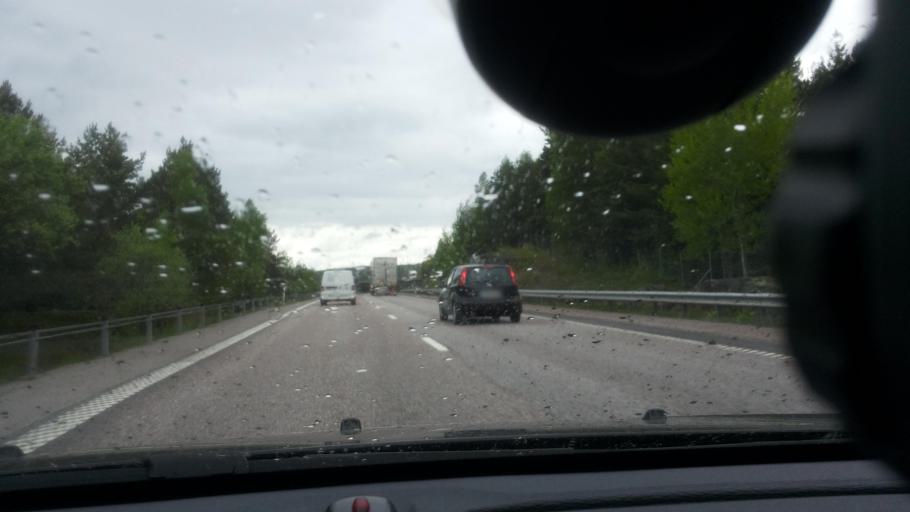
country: SE
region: Stockholm
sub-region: Sigtuna Kommun
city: Marsta
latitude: 59.6699
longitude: 17.8750
